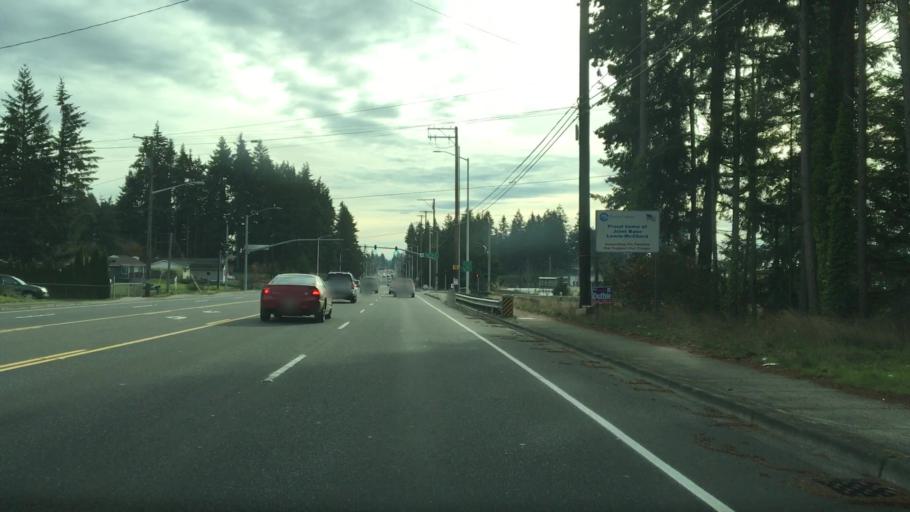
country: US
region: Washington
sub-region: Pierce County
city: South Hill
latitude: 47.1468
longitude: -122.3041
